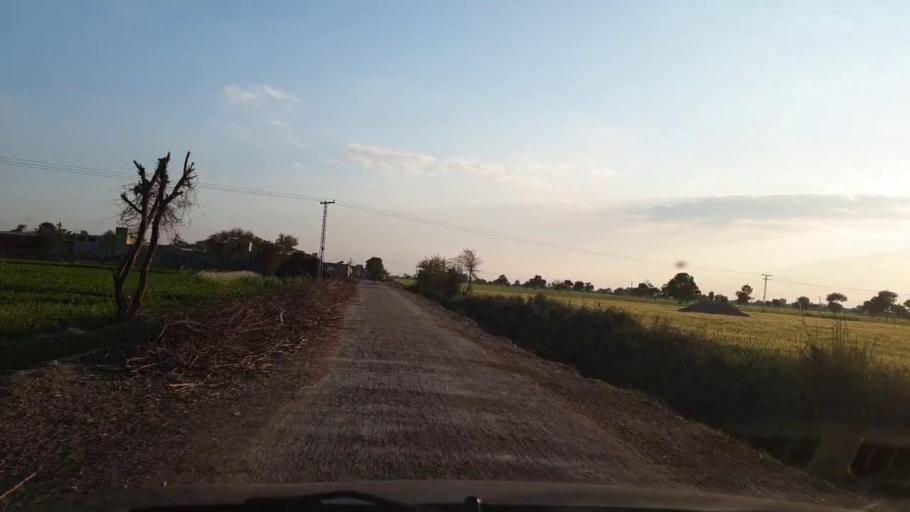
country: PK
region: Sindh
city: Sinjhoro
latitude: 25.9984
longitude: 68.8014
